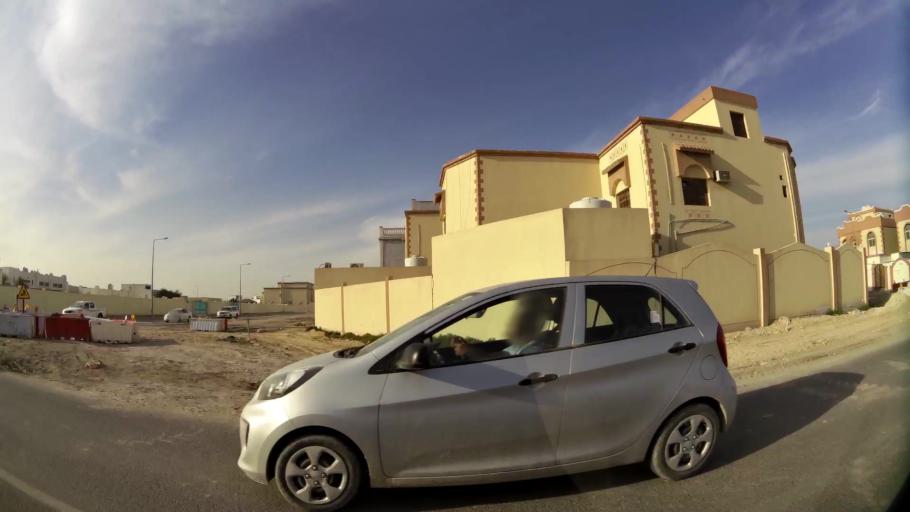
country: QA
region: Al Wakrah
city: Al Wakrah
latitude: 25.1443
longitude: 51.6064
